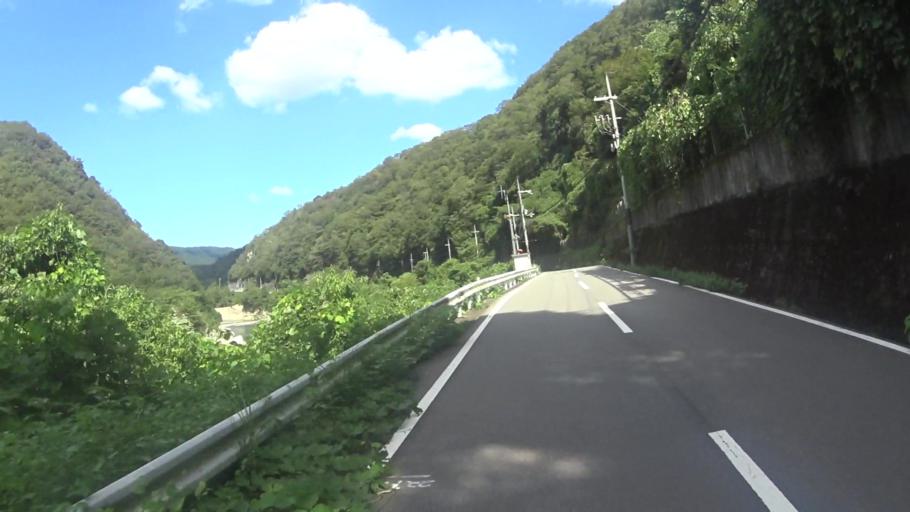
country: JP
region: Mie
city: Ueno-ebisumachi
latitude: 34.7595
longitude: 136.0019
